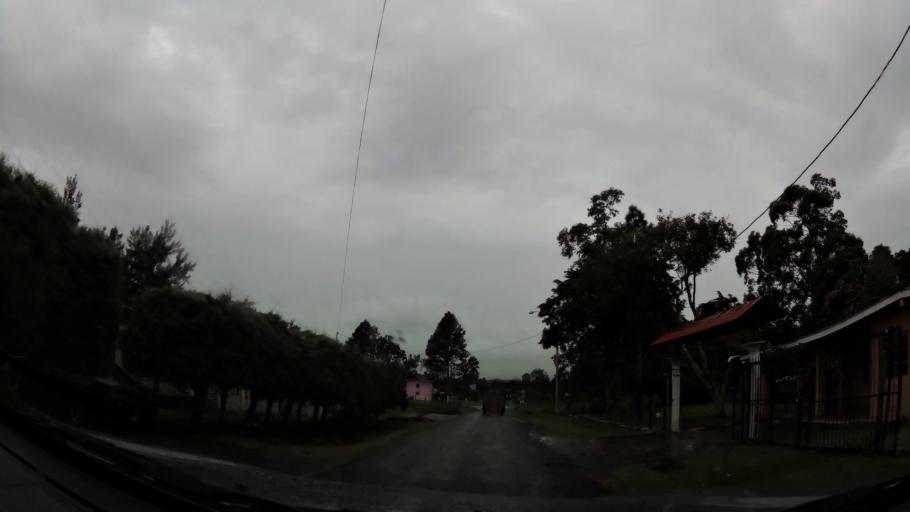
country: PA
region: Chiriqui
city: Volcan
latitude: 8.7896
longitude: -82.6488
